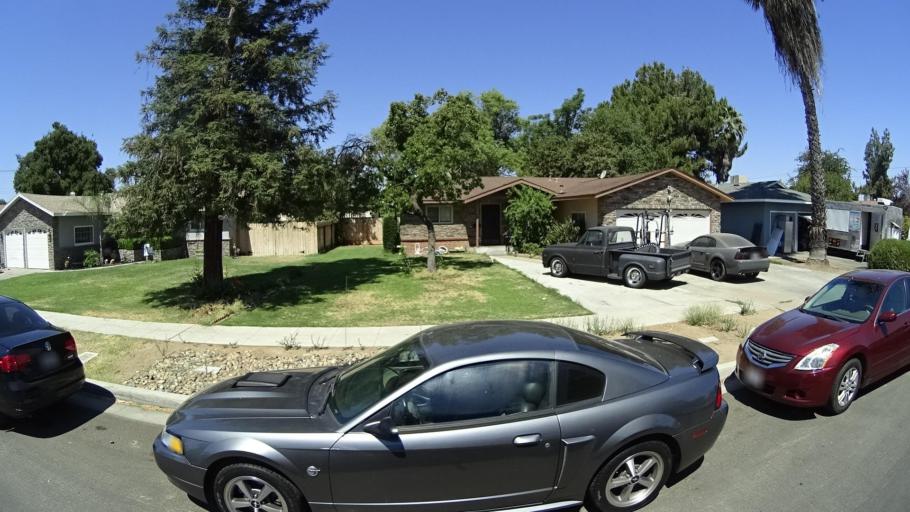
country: US
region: California
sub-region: Fresno County
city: Fresno
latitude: 36.7636
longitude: -119.7516
